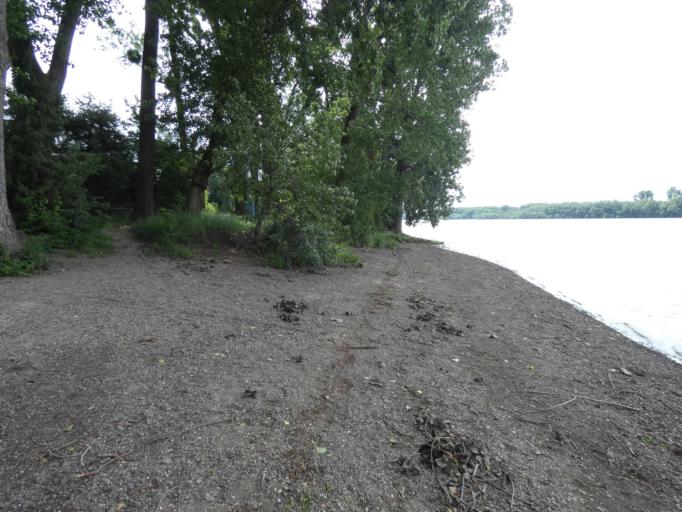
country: HU
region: Pest
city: Kismaros
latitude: 47.8215
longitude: 19.0124
